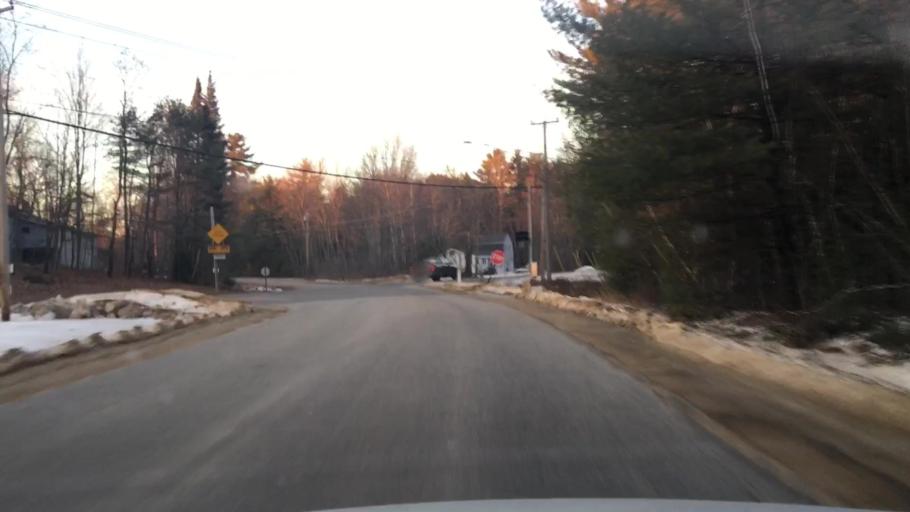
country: US
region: Maine
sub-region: York County
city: Lebanon
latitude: 43.3802
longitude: -70.8773
